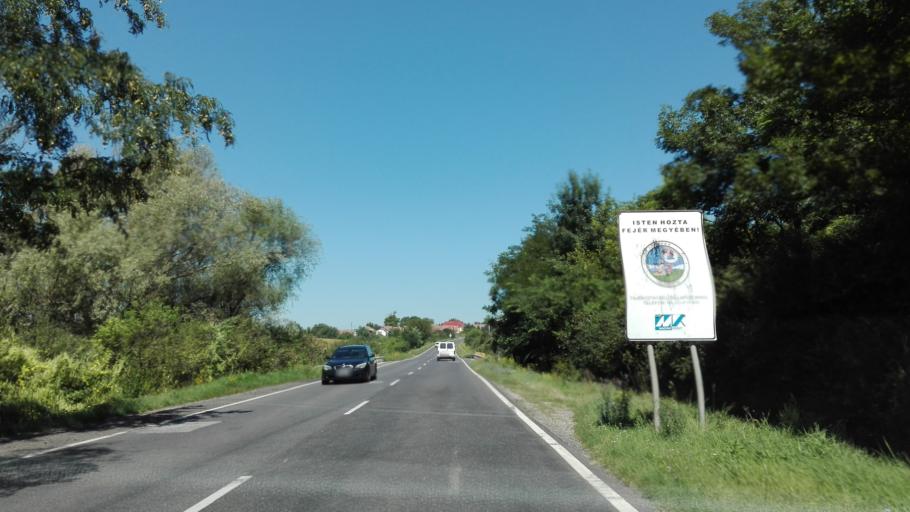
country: HU
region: Tolna
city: Simontornya
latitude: 46.7683
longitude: 18.5196
